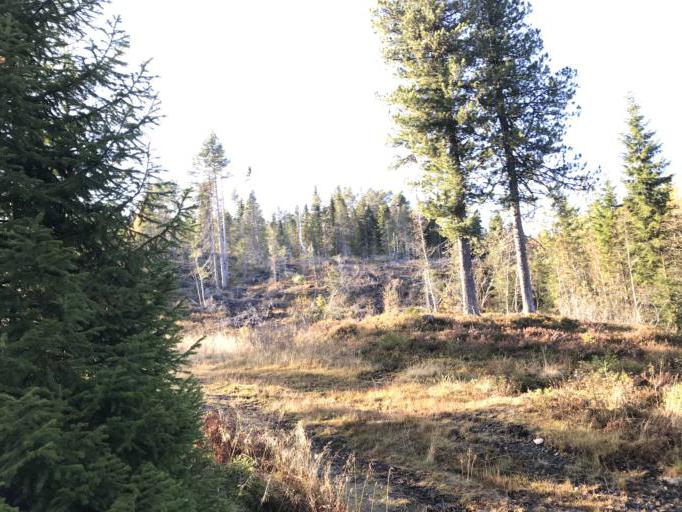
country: NO
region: Sor-Trondelag
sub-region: Trondheim
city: Trondheim
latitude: 63.4141
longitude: 10.3290
